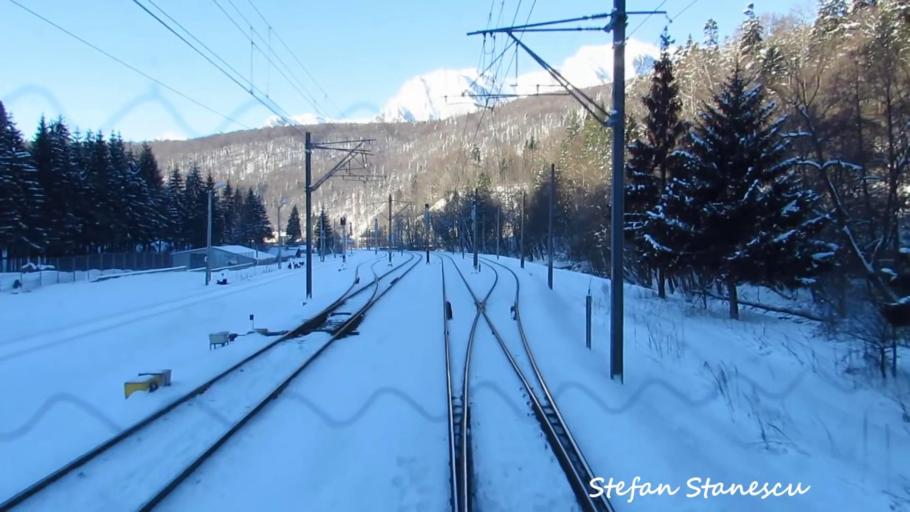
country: RO
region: Prahova
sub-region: Oras Azuga
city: Azuga
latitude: 45.4501
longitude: 25.5587
